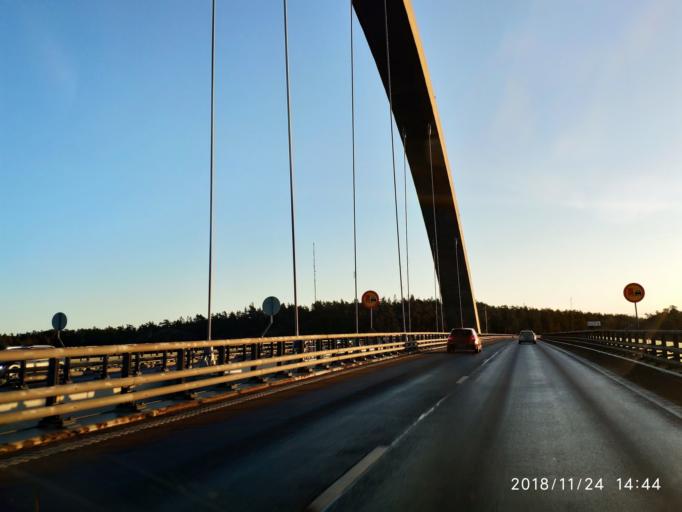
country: NO
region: Ostfold
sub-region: Sarpsborg
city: Skjeberg
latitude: 59.0949
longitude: 11.2515
